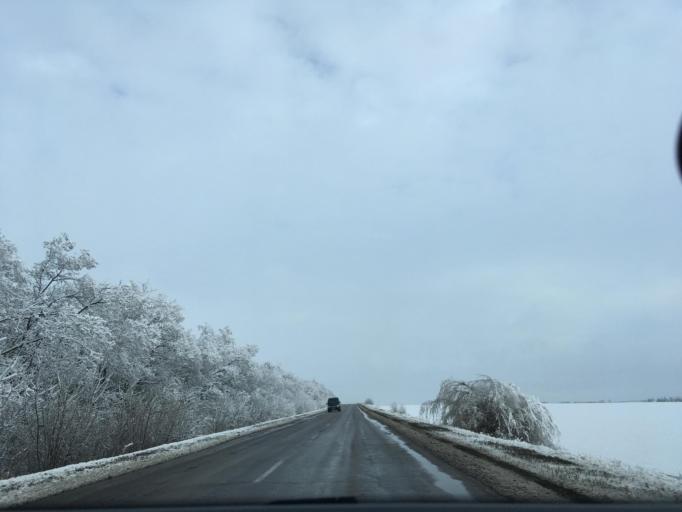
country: UA
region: Luhansk
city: Lozno-Oleksandrivka
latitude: 49.9903
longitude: 39.0198
